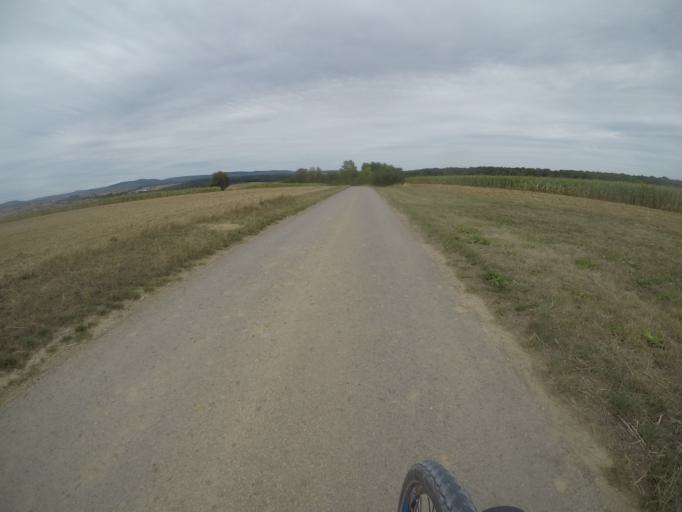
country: DE
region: Baden-Wuerttemberg
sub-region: Regierungsbezirk Stuttgart
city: Oberriexingen
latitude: 48.9189
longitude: 9.0335
